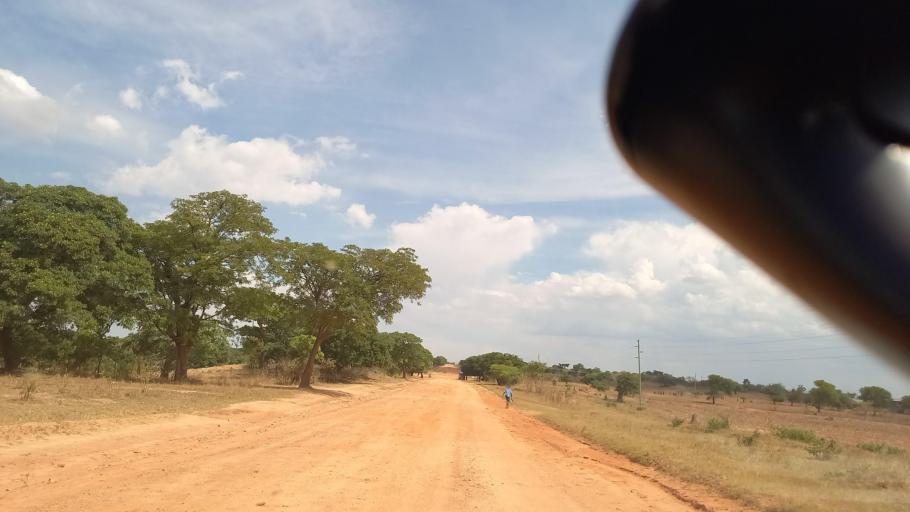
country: ZM
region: Lusaka
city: Kafue
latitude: -16.1326
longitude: 28.0487
